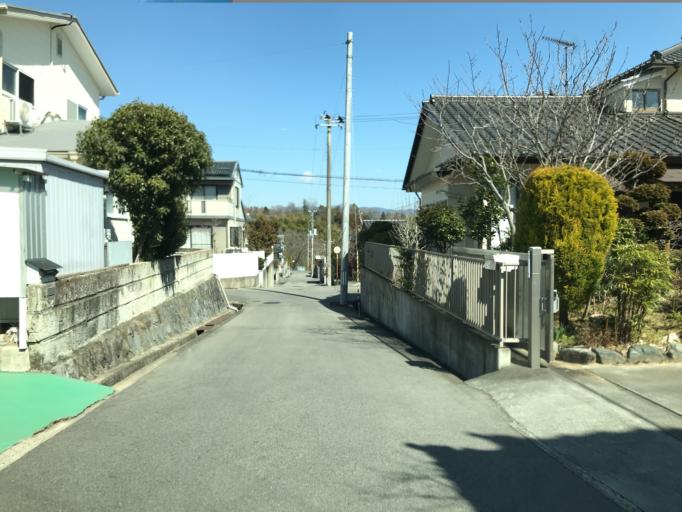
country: JP
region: Fukushima
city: Iwaki
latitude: 37.0477
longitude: 140.8524
